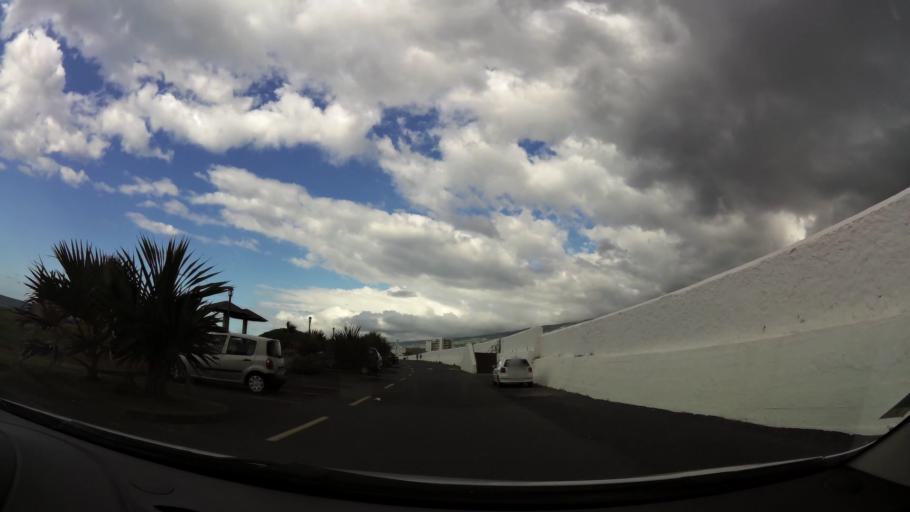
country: RE
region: Reunion
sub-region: Reunion
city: Saint-Denis
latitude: -20.8820
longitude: 55.4645
